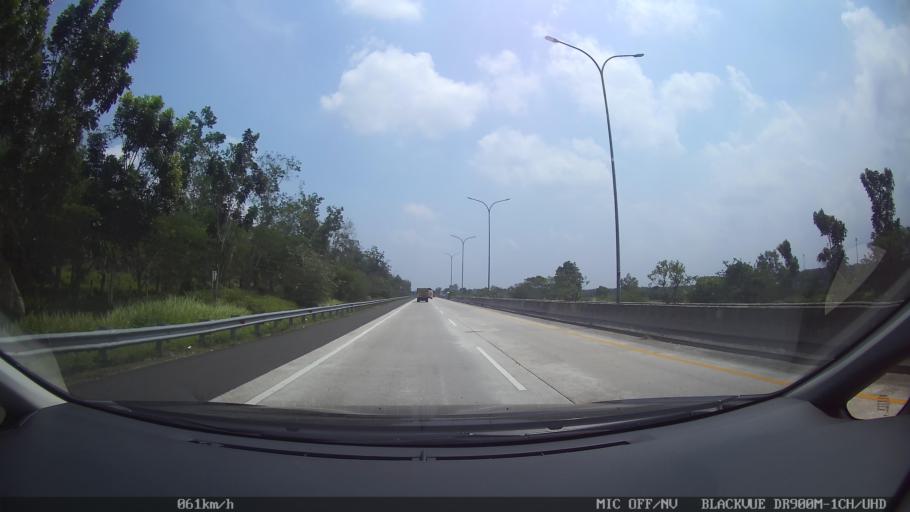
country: ID
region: Lampung
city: Kedaton
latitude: -5.3613
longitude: 105.3251
